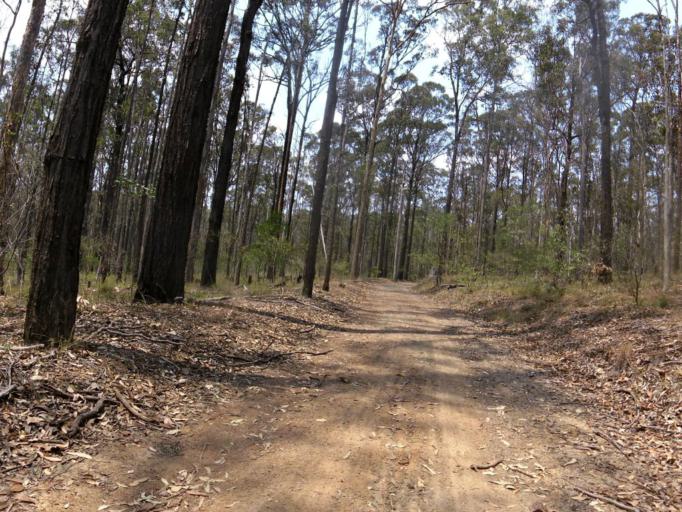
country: AU
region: Queensland
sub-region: Logan
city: Springwood
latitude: -27.6100
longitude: 153.1578
